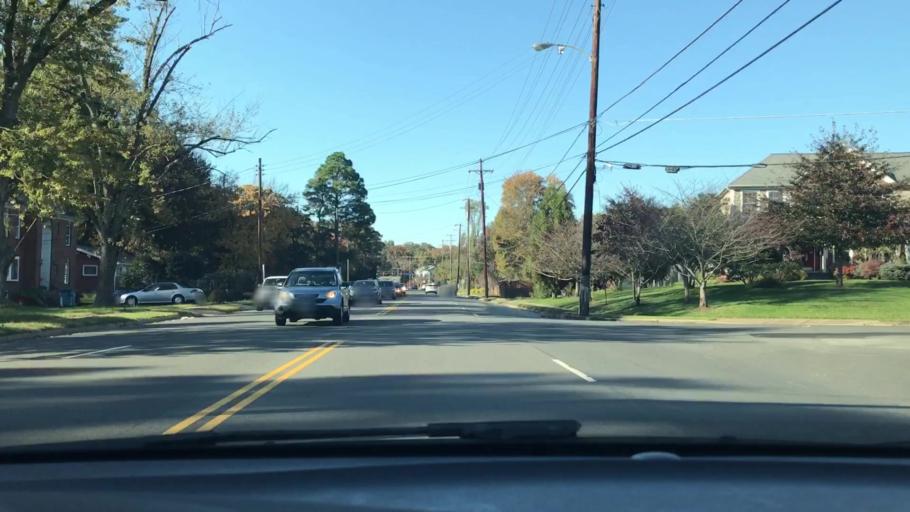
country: US
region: Virginia
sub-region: Fairfax County
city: Annandale
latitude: 38.8439
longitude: -77.2010
